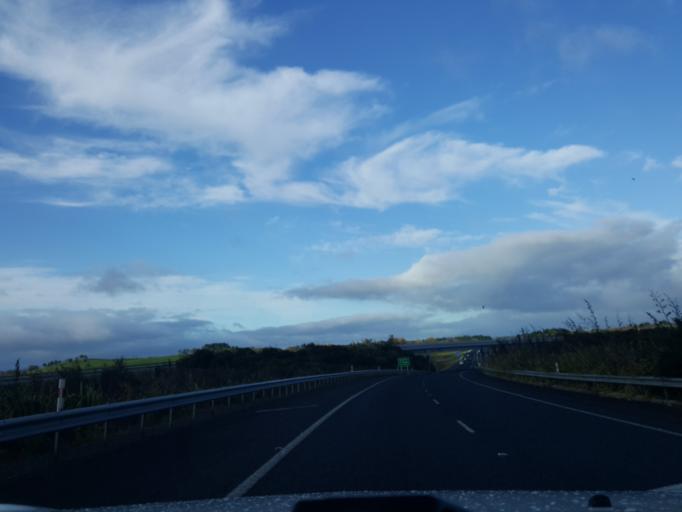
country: NZ
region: Waikato
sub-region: Waikato District
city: Ngaruawahia
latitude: -37.6843
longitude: 175.2160
